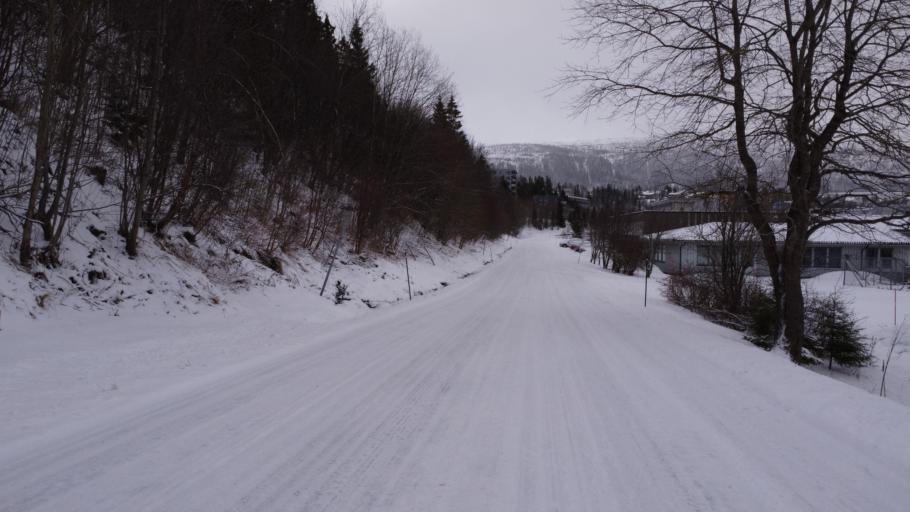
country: NO
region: Nordland
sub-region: Rana
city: Mo i Rana
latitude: 66.3228
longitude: 14.1544
